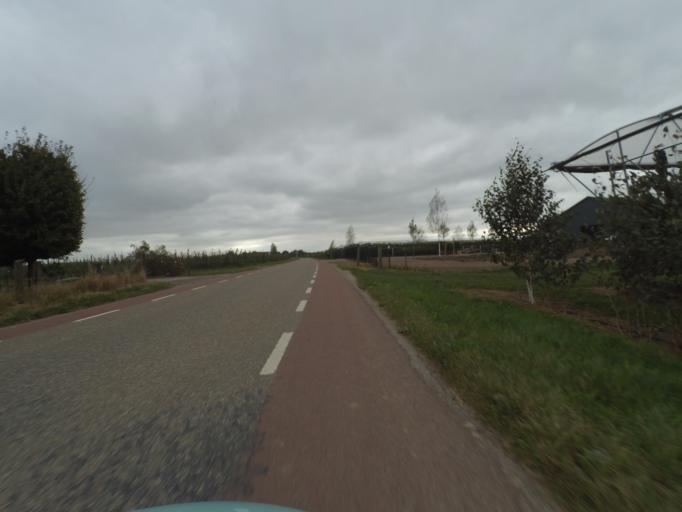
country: NL
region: Utrecht
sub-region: Gemeente Rhenen
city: Rhenen
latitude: 51.9450
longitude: 5.5463
